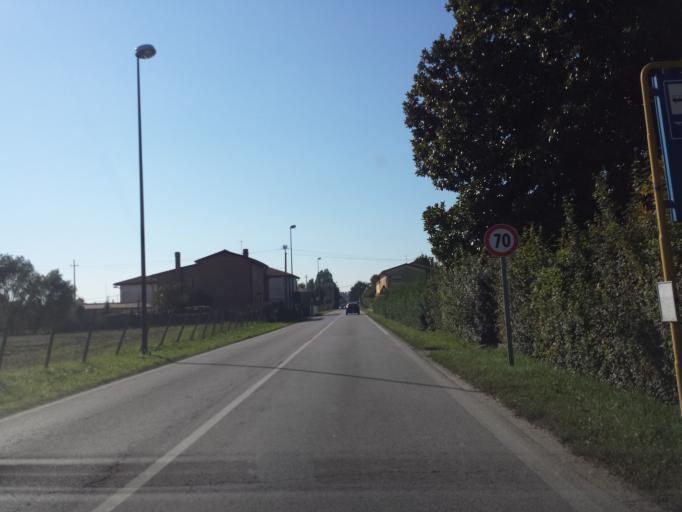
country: IT
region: Veneto
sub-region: Provincia di Vicenza
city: Camisano Vicentino
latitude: 45.5418
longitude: 11.7198
